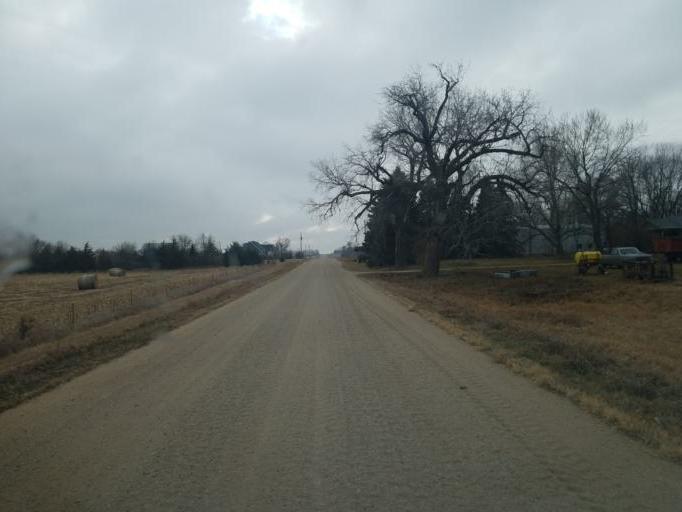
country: US
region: Nebraska
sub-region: Knox County
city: Creighton
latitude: 42.4591
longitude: -97.7984
